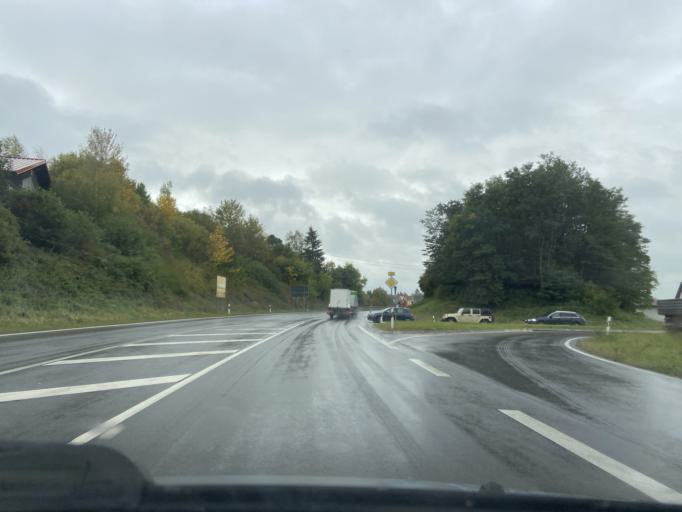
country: DE
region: Baden-Wuerttemberg
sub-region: Tuebingen Region
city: Messkirch
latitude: 48.0006
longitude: 9.1182
